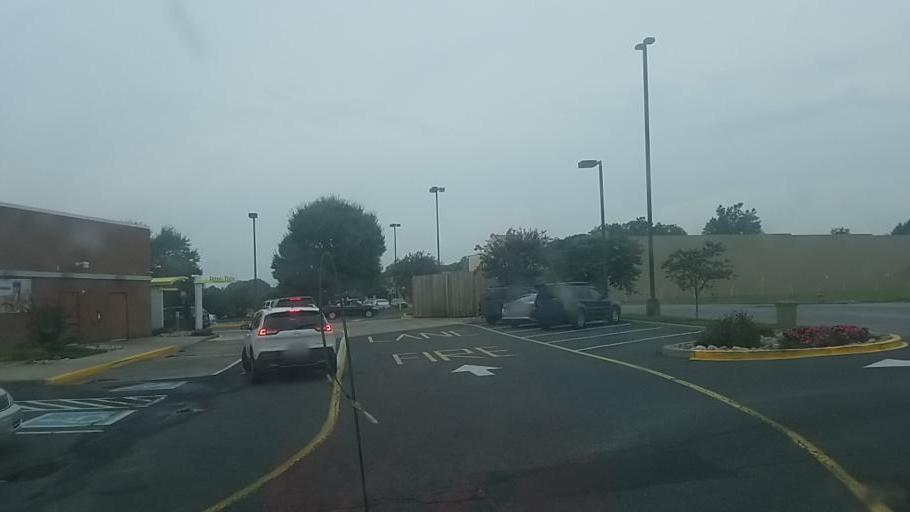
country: US
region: Maryland
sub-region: Wicomico County
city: Salisbury
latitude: 38.3672
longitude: -75.5480
